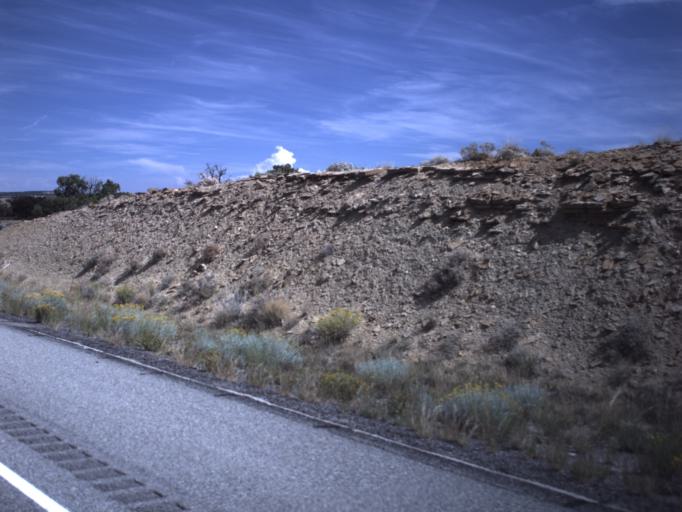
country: US
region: Utah
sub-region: Emery County
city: Castle Dale
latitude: 38.8692
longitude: -110.6971
